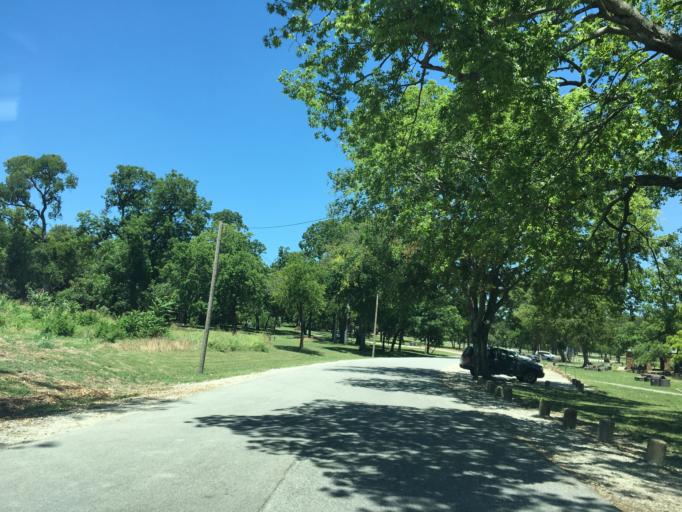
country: US
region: Texas
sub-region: Dallas County
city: Highland Park
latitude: 32.8378
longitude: -96.7097
